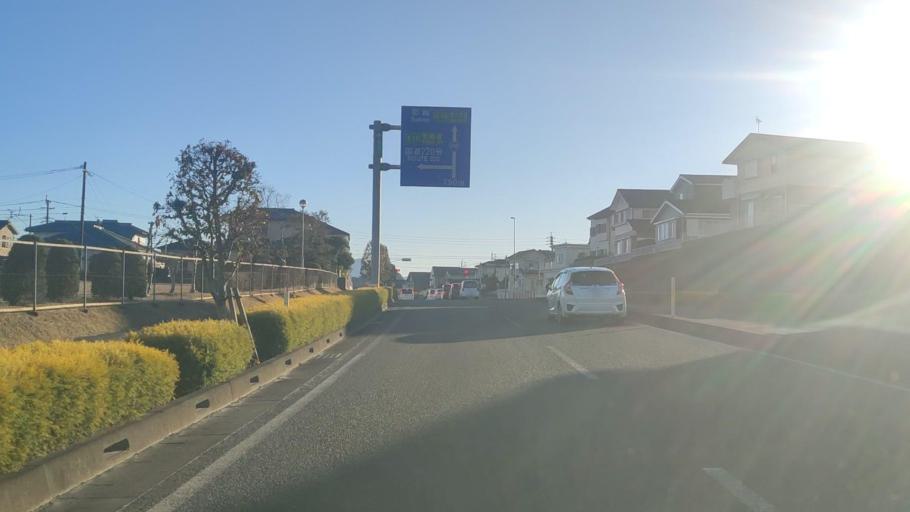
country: JP
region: Miyazaki
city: Miyazaki-shi
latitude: 31.8781
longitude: 131.3923
